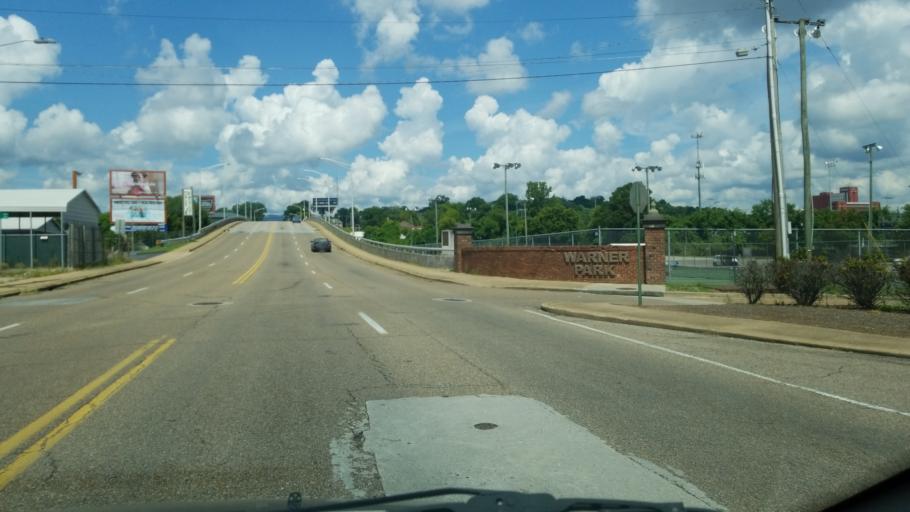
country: US
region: Tennessee
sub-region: Hamilton County
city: Chattanooga
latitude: 35.0397
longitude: -85.2850
